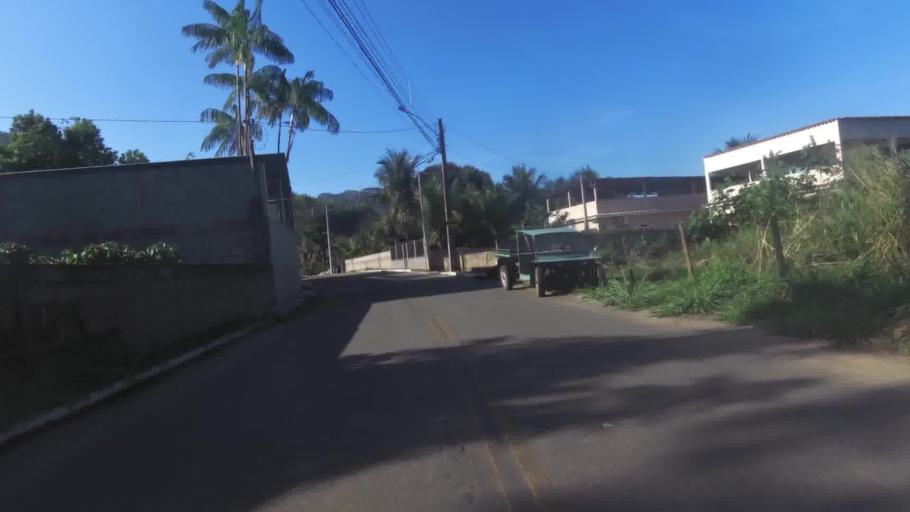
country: BR
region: Espirito Santo
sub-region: Iconha
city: Iconha
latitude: -20.7364
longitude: -40.7833
